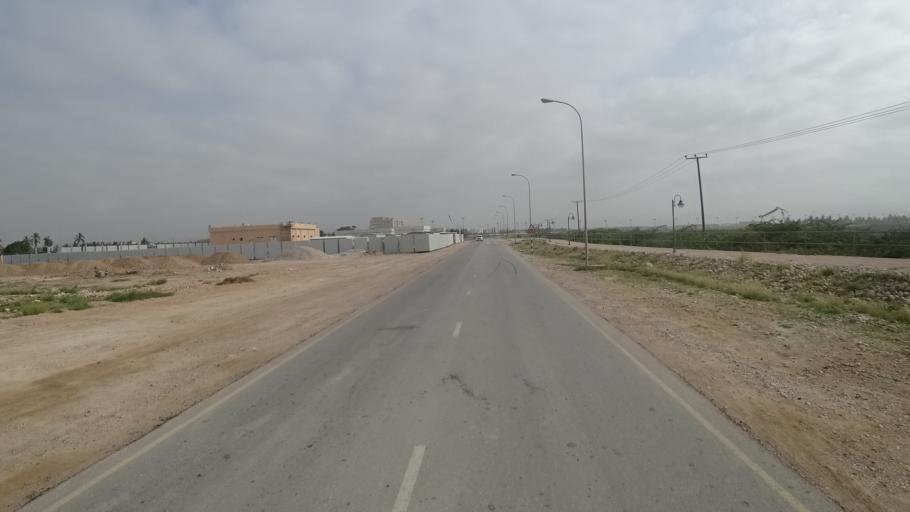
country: OM
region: Zufar
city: Salalah
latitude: 17.0207
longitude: 54.1741
